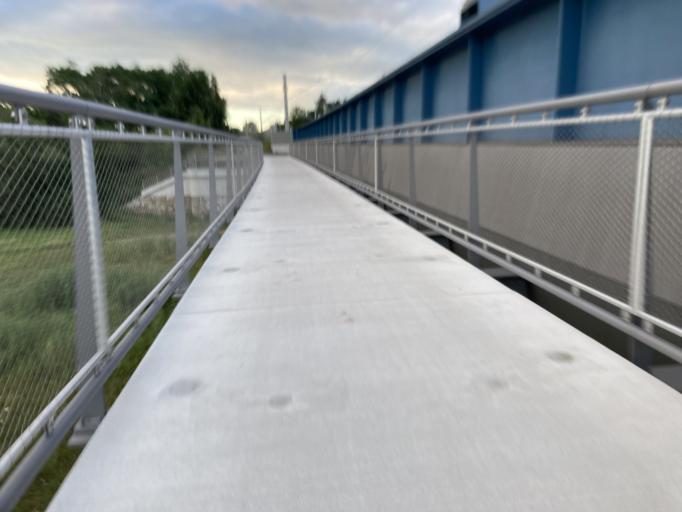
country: DE
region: Lower Saxony
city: Verden
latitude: 52.9084
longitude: 9.2413
